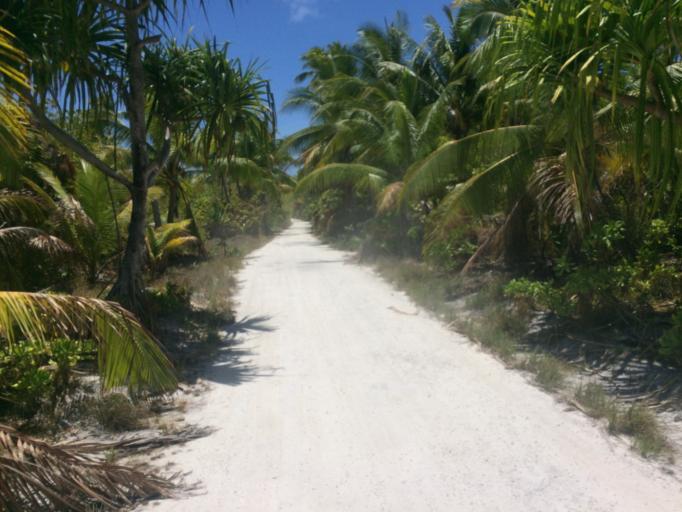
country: KI
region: Gilbert Islands
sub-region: Marakei
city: Rawannawi Village
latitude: 1.7685
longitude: 173.0452
